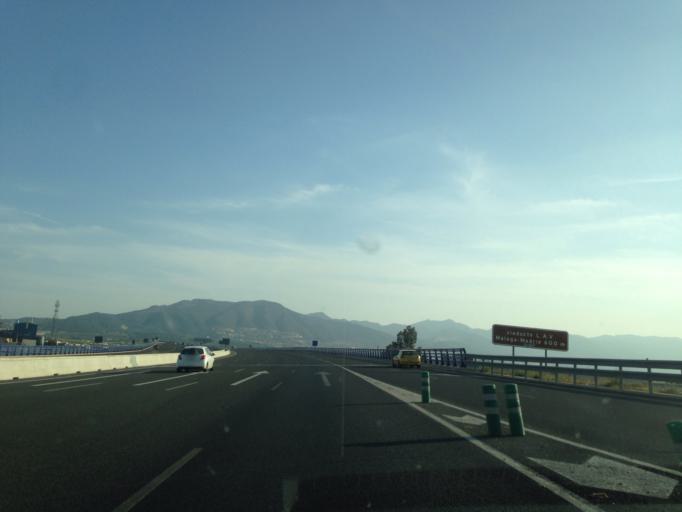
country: ES
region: Andalusia
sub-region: Provincia de Malaga
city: Alhaurin de la Torre
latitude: 36.7074
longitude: -4.5135
